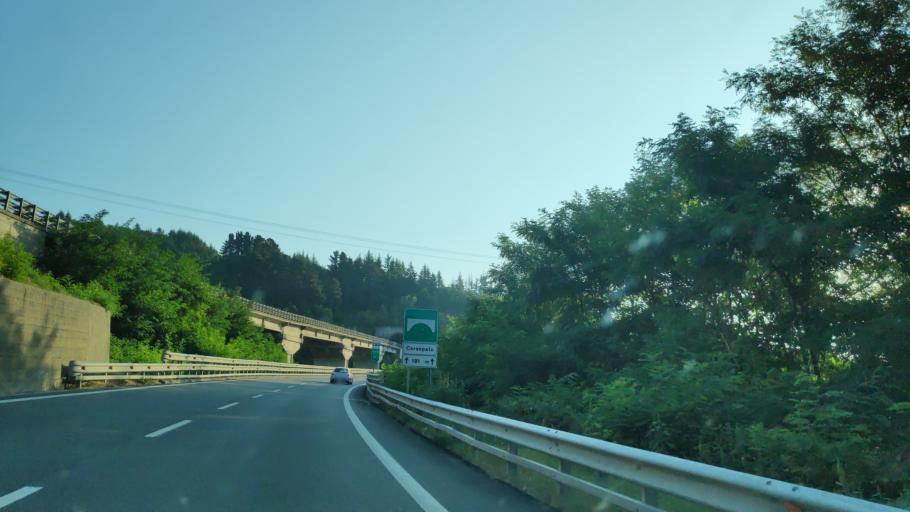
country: IT
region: Calabria
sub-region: Provincia di Cosenza
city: Belsito
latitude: 39.1626
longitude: 16.2879
